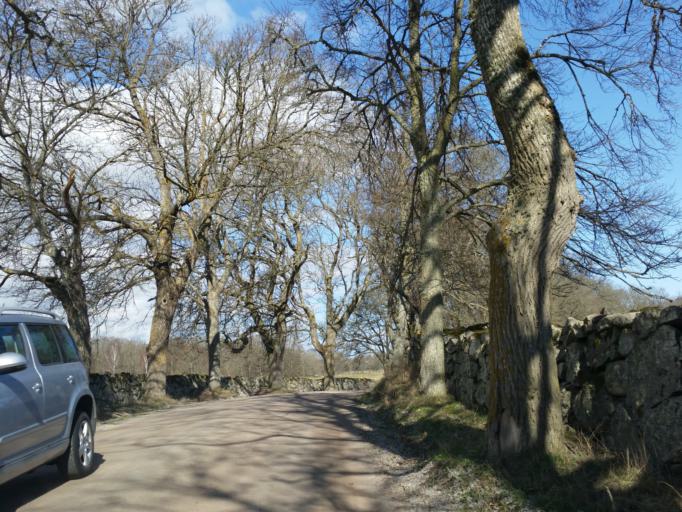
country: SE
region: Kalmar
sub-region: Monsteras Kommun
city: Timmernabben
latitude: 56.9396
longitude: 16.4238
